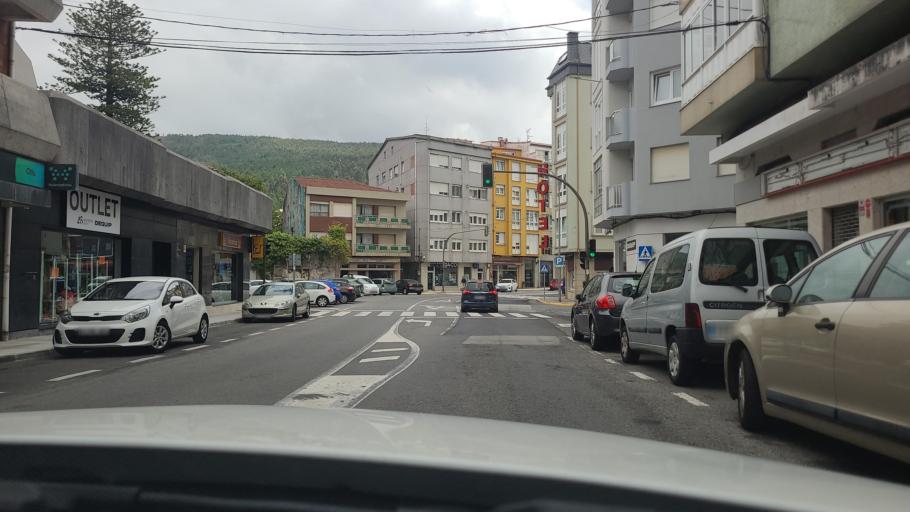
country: ES
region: Galicia
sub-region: Provincia da Coruna
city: Cee
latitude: 42.9576
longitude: -9.1916
